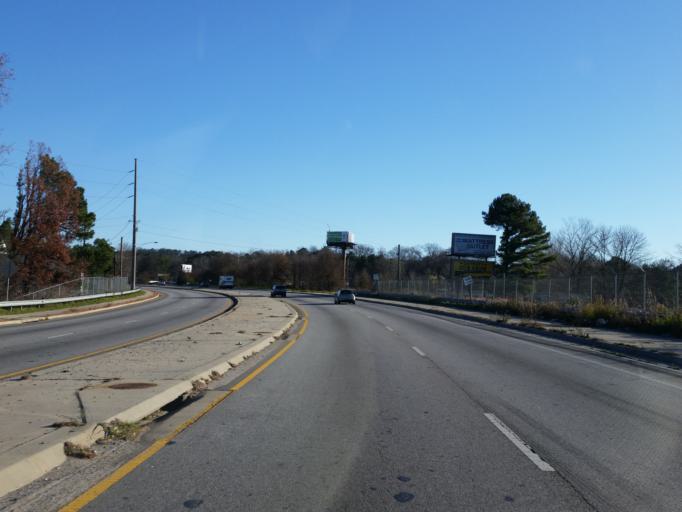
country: US
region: Georgia
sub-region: Cobb County
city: Vinings
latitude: 33.8239
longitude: -84.4578
